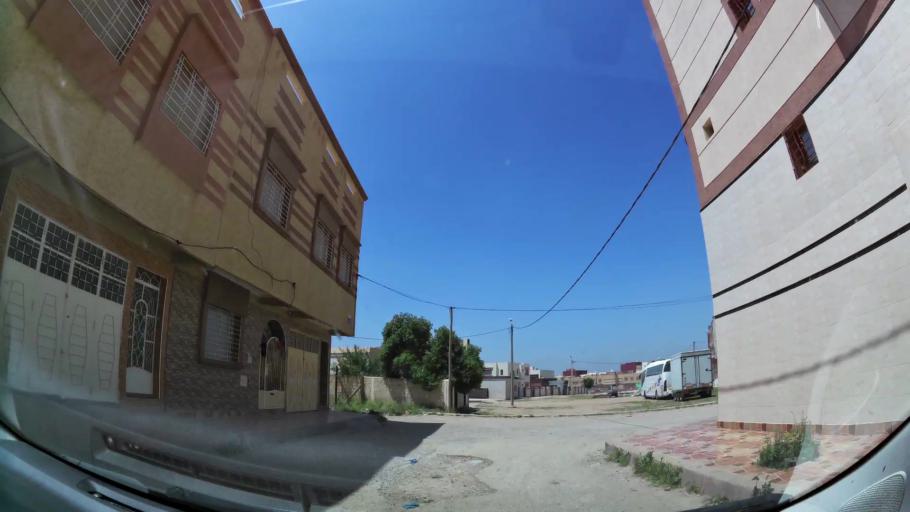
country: MA
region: Oriental
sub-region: Oujda-Angad
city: Oujda
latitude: 34.6943
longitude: -1.8895
